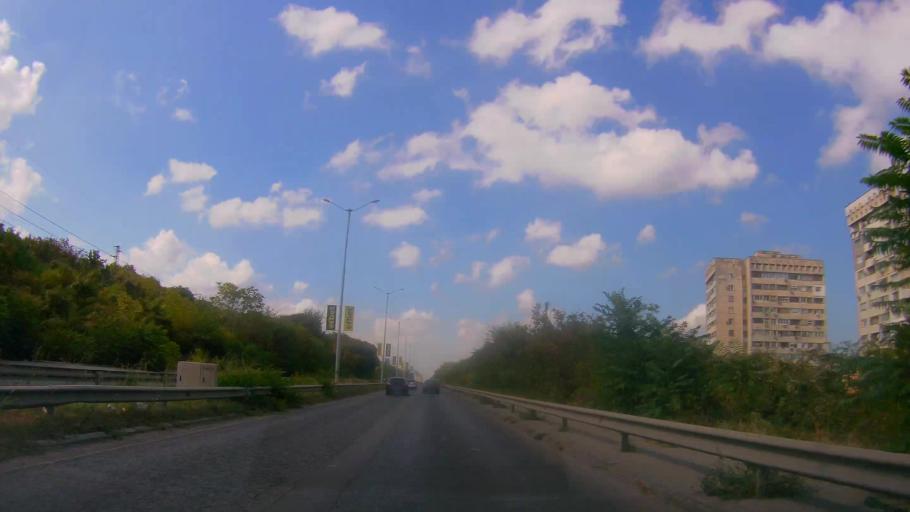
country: BG
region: Ruse
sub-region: Obshtina Ruse
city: Ruse
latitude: 43.8502
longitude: 25.9997
